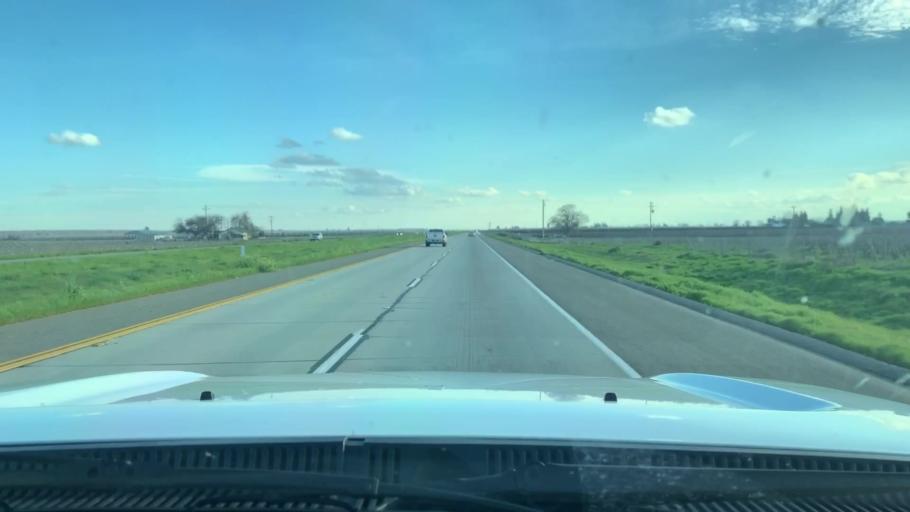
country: US
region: California
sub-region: Fresno County
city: Easton
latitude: 36.5929
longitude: -119.7862
